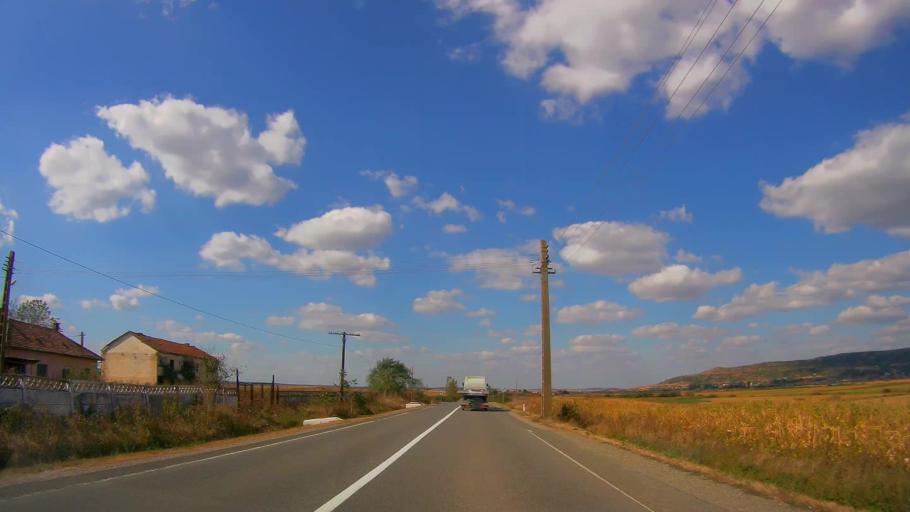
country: RO
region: Salaj
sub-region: Comuna Bobota
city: Dersida
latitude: 47.3659
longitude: 22.7917
